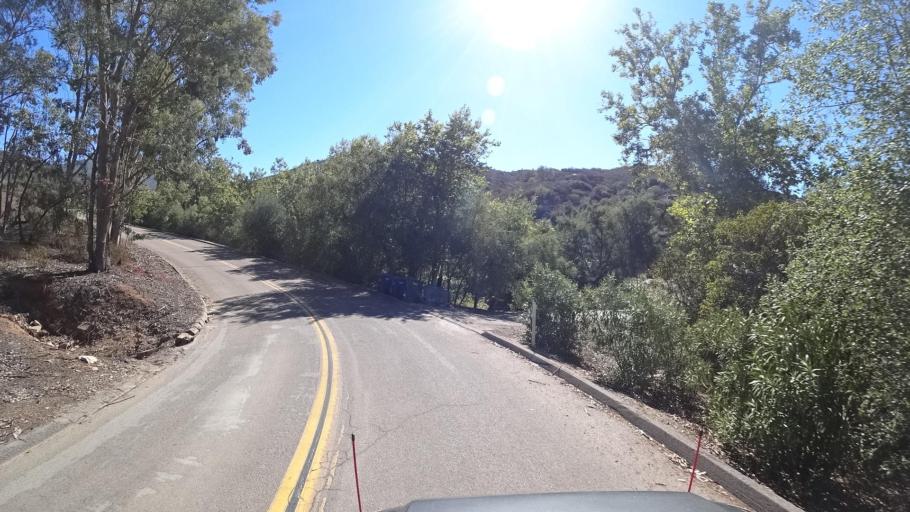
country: US
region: California
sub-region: San Diego County
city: Alpine
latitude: 32.8589
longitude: -116.7712
